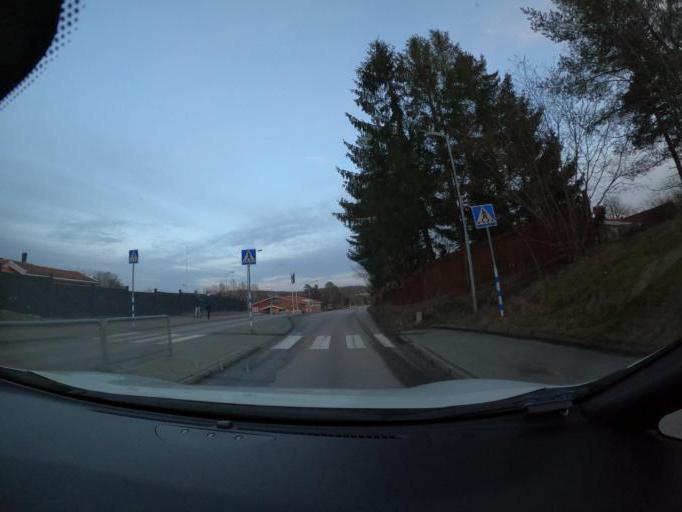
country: SE
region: Vaestra Goetaland
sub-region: Harryda Kommun
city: Molnlycke
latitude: 57.6533
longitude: 12.1365
